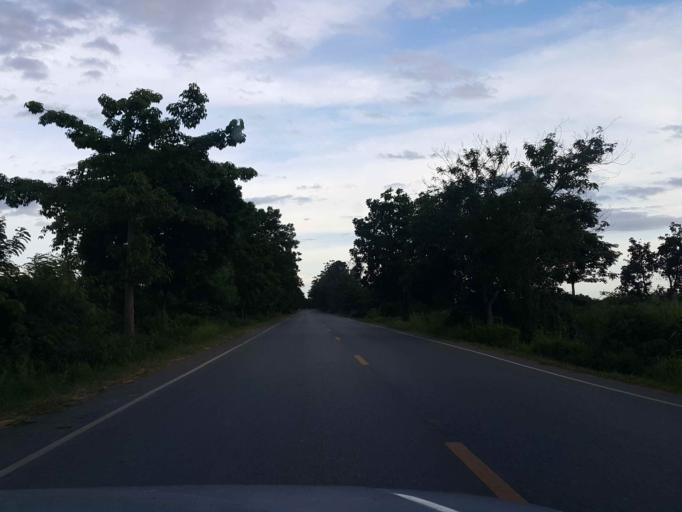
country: TH
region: Sukhothai
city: Sawankhalok
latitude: 17.3772
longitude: 99.7387
